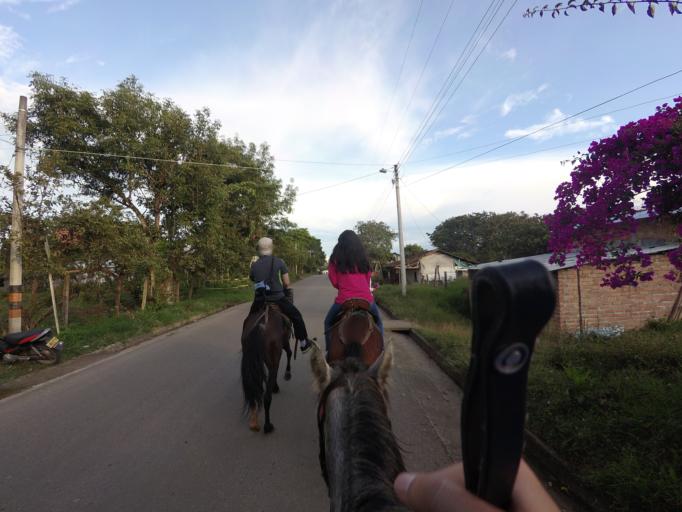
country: CO
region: Huila
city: San Agustin
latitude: 1.8962
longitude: -76.2748
